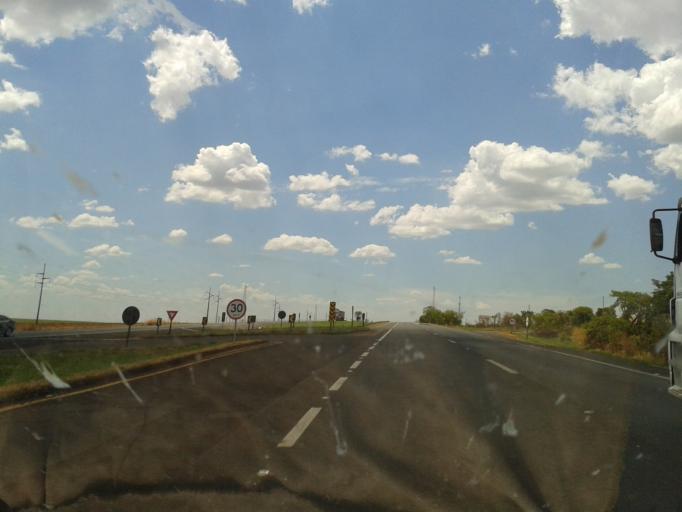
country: BR
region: Minas Gerais
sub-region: Uberlandia
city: Uberlandia
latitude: -19.0789
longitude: -48.1877
